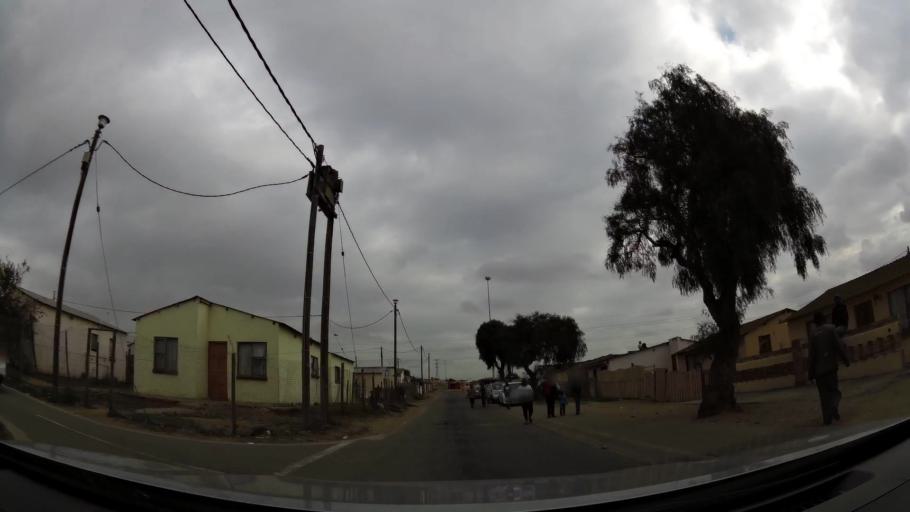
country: ZA
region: Eastern Cape
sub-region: Nelson Mandela Bay Metropolitan Municipality
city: Port Elizabeth
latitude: -33.8890
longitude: 25.5961
